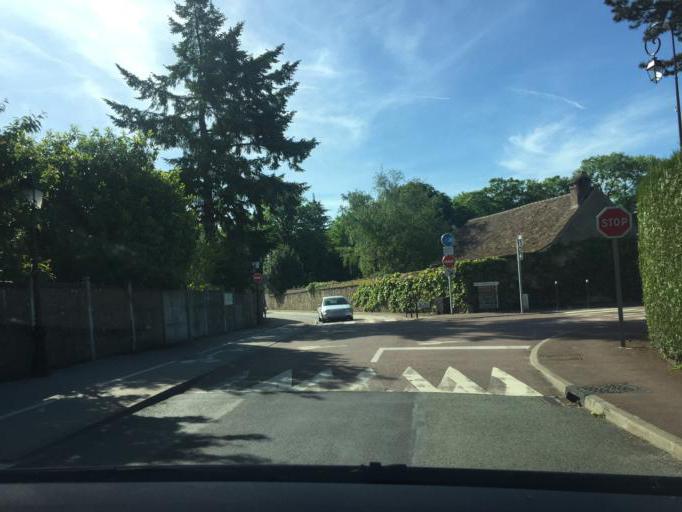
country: FR
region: Ile-de-France
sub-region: Departement des Yvelines
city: Les Loges-en-Josas
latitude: 48.7655
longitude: 2.1383
